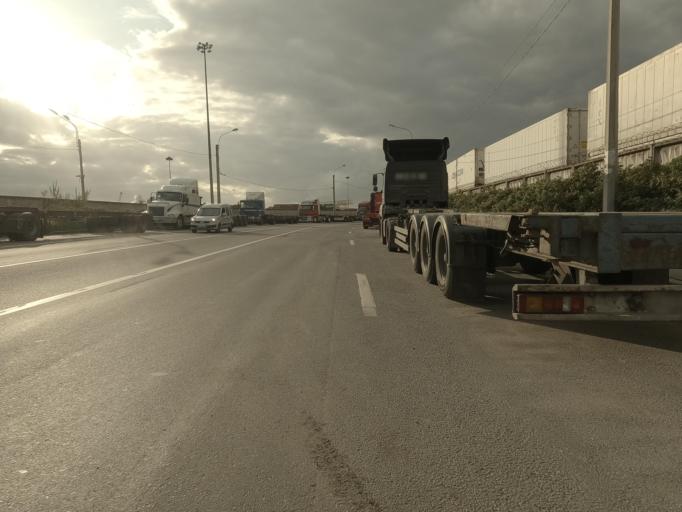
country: RU
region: St.-Petersburg
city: Avtovo
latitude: 59.8660
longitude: 30.2390
